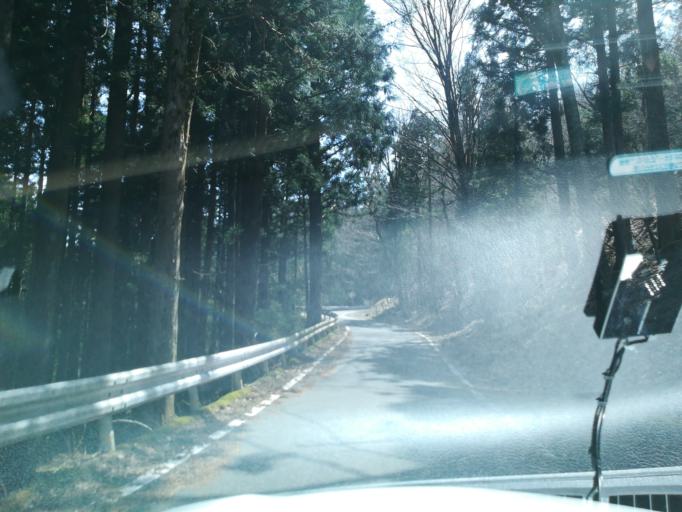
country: JP
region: Tokushima
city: Wakimachi
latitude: 33.8829
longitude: 134.0611
